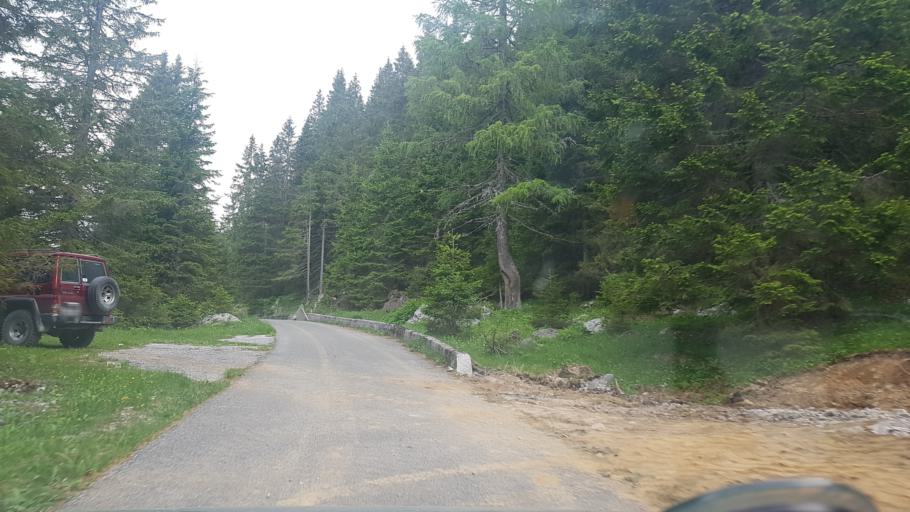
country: IT
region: Friuli Venezia Giulia
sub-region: Provincia di Udine
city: Paularo
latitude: 46.5570
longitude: 13.1884
